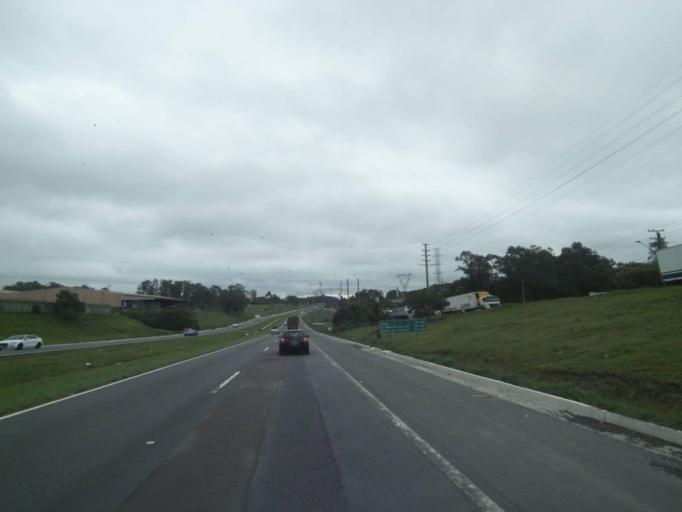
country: BR
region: Parana
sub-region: Sao Jose Dos Pinhais
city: Sao Jose dos Pinhais
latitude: -25.5429
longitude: -49.3138
